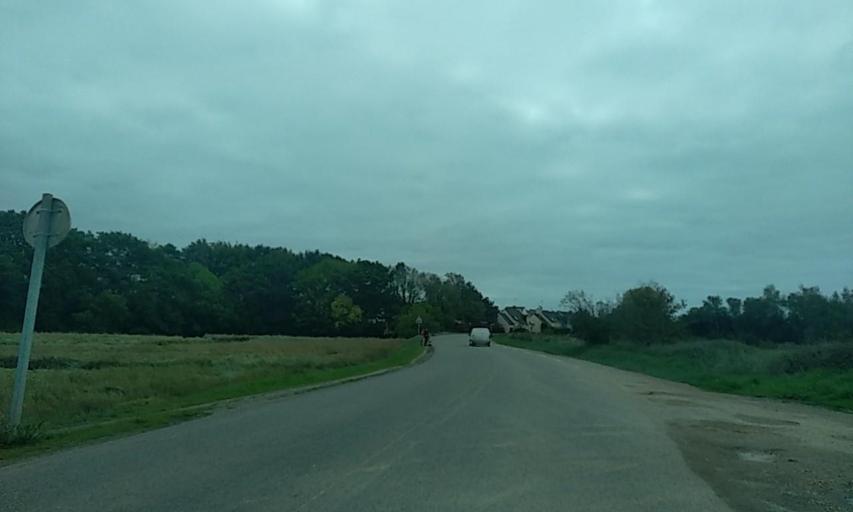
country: FR
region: Brittany
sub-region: Departement du Morbihan
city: Lorient
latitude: 47.7713
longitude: -3.3610
